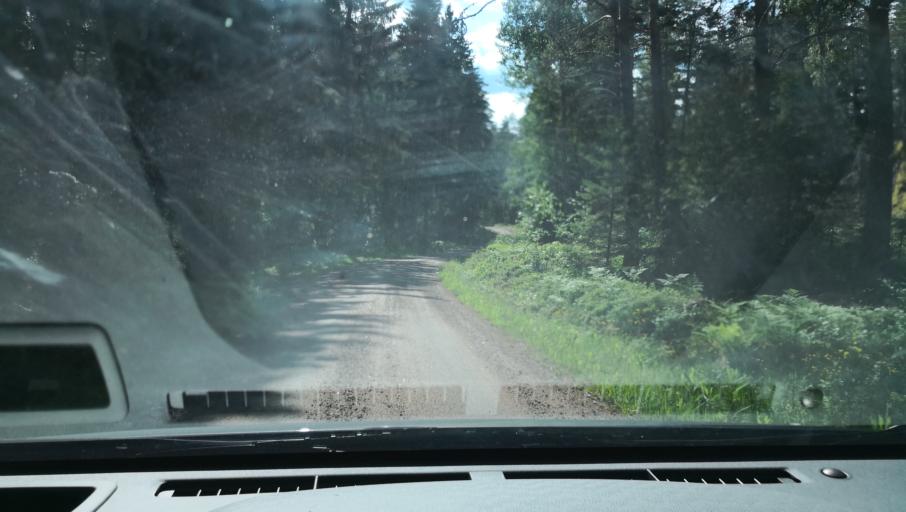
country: SE
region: Uppsala
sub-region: Enkopings Kommun
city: Orsundsbro
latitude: 59.8382
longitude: 17.2650
